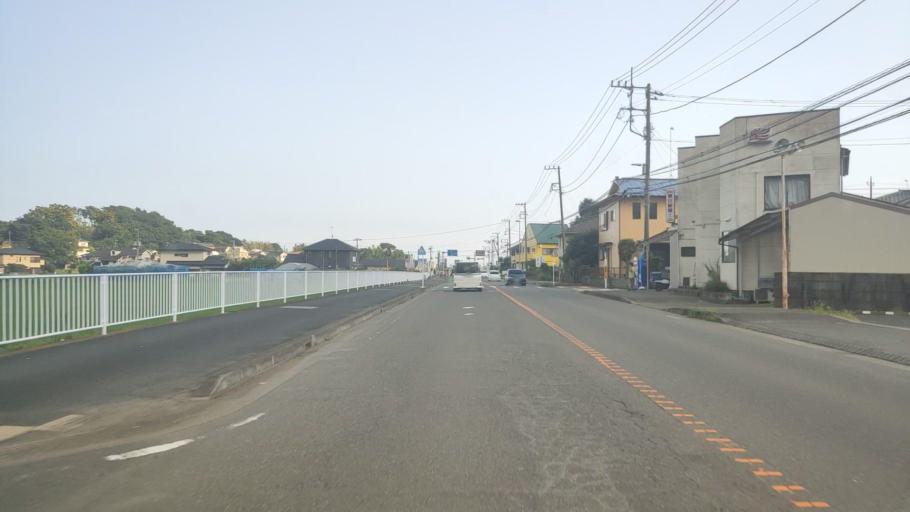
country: JP
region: Kanagawa
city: Isehara
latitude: 35.3812
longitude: 139.3171
